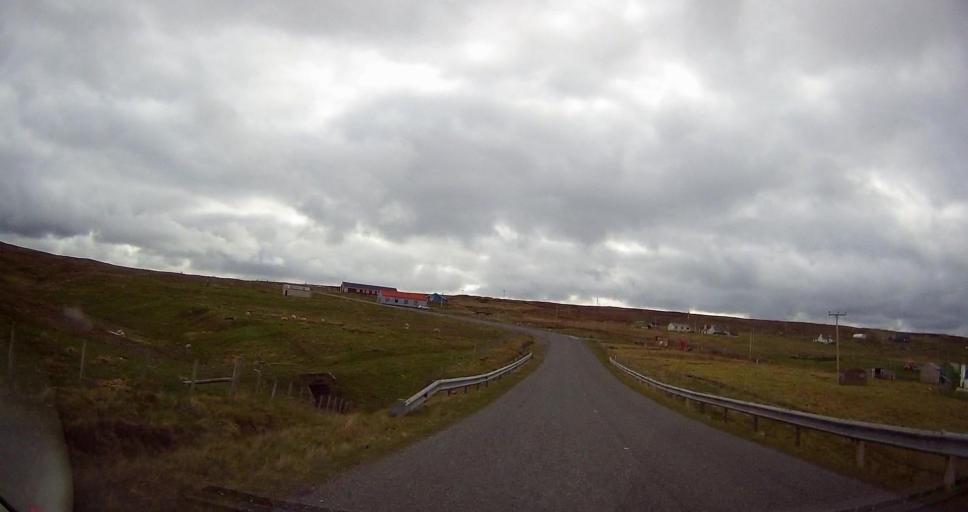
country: GB
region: Scotland
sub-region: Shetland Islands
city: Shetland
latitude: 60.6617
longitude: -1.0500
